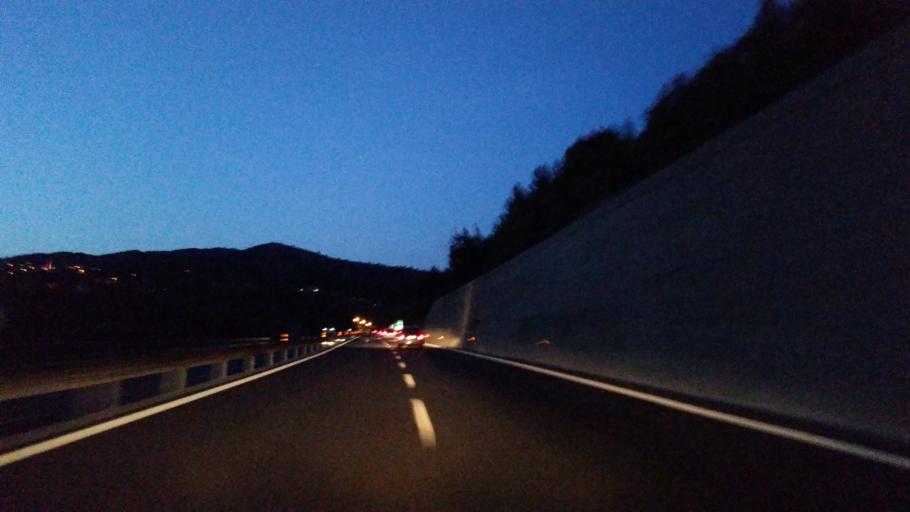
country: IT
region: Liguria
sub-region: Provincia di Imperia
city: Cervo
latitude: 43.9372
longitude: 8.1074
